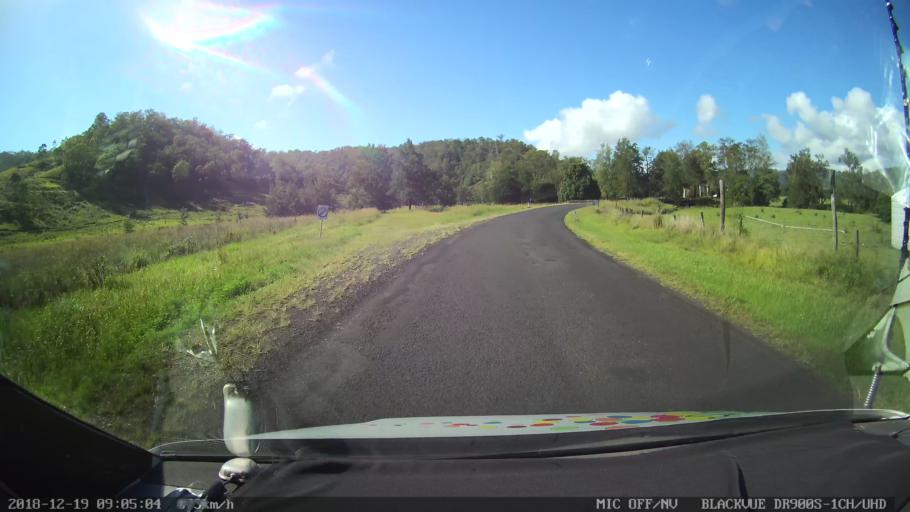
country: AU
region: New South Wales
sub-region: Kyogle
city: Kyogle
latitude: -28.4612
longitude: 152.9455
